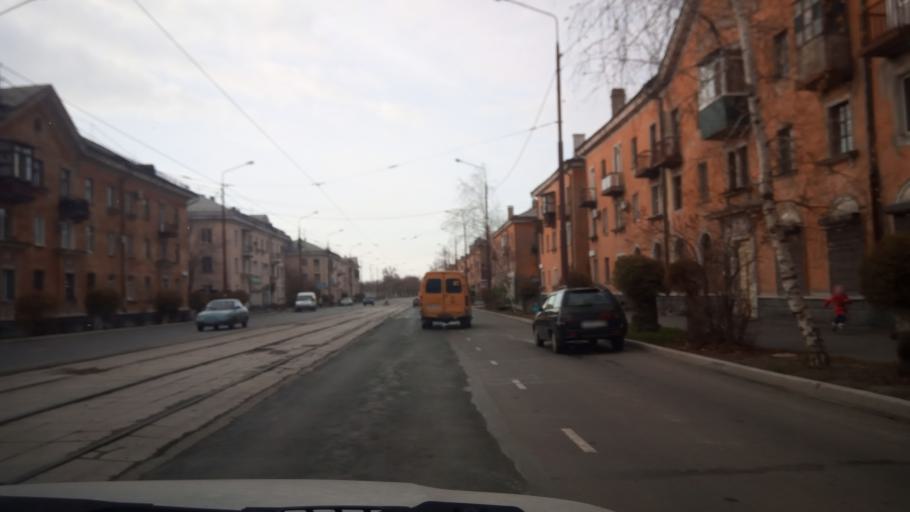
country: RU
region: Orenburg
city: Novotroitsk
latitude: 51.1983
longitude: 58.3328
